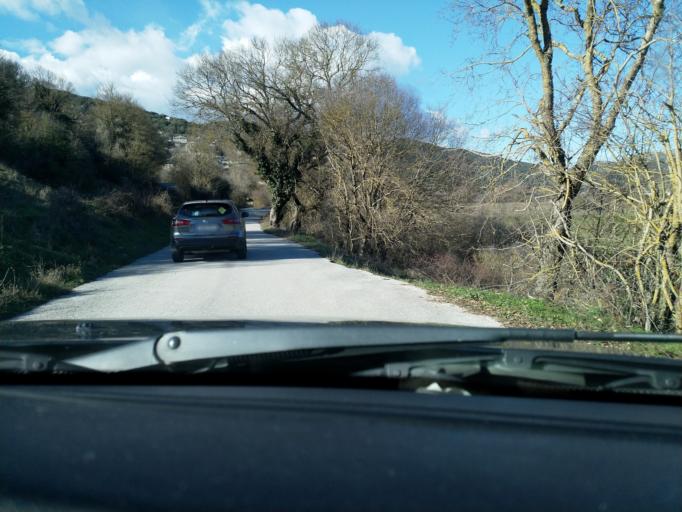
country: GR
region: Epirus
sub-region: Nomos Ioanninon
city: Kalpaki
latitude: 39.8782
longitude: 20.6811
